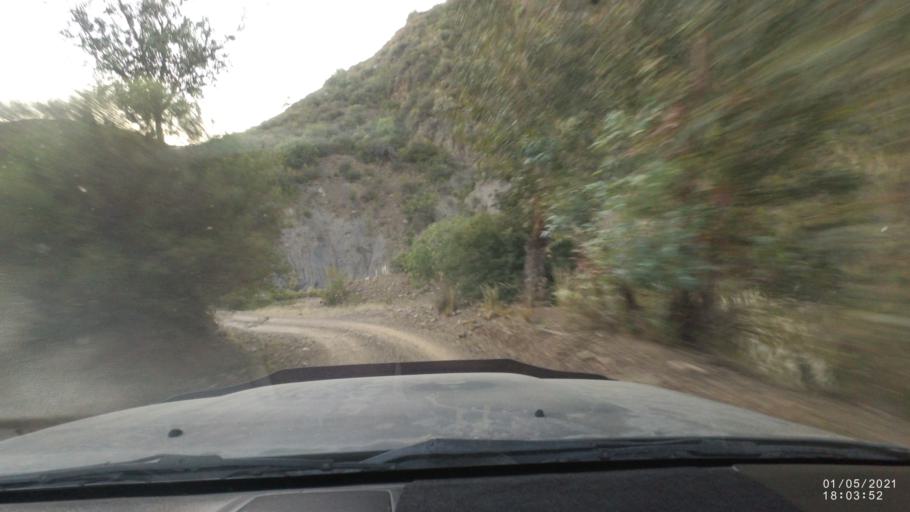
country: BO
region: Cochabamba
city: Capinota
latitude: -17.6886
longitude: -66.1780
